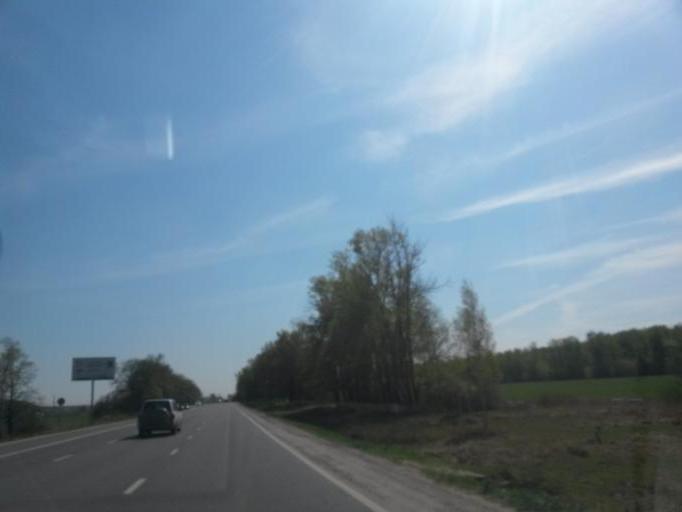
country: RU
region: Moskovskaya
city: L'vovskiy
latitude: 55.3388
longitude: 37.5282
